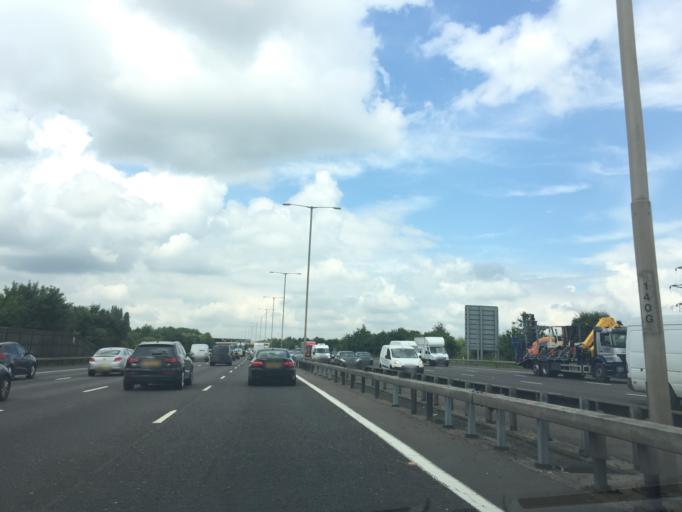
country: GB
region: England
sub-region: Buckinghamshire
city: Iver
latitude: 51.5243
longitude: -0.4984
